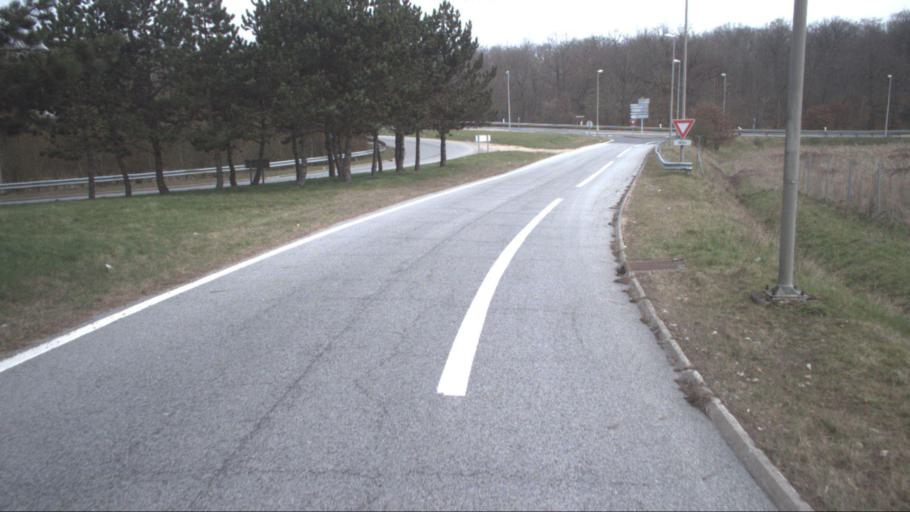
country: FR
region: Ile-de-France
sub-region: Departement des Yvelines
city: Rambouillet
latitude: 48.6193
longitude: 1.8316
